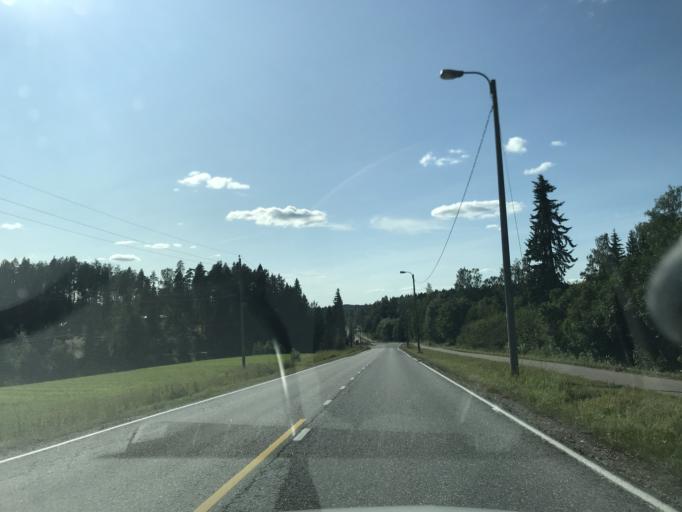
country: FI
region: Uusimaa
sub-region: Helsinki
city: Nurmijaervi
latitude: 60.3815
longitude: 24.6655
